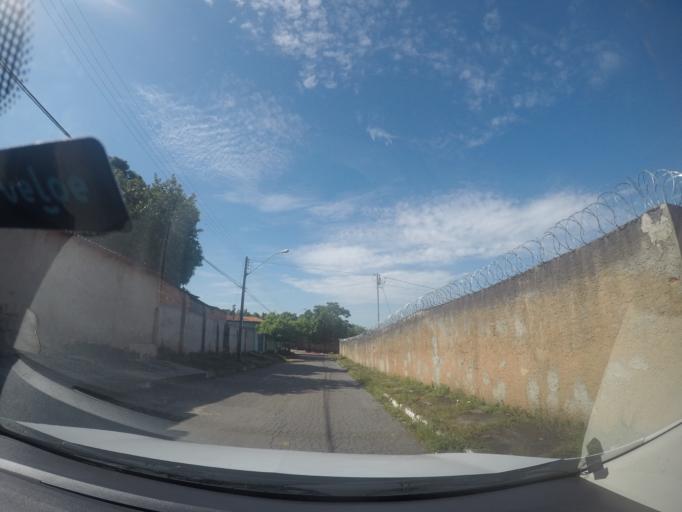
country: BR
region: Goias
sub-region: Goiania
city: Goiania
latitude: -16.6625
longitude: -49.1972
